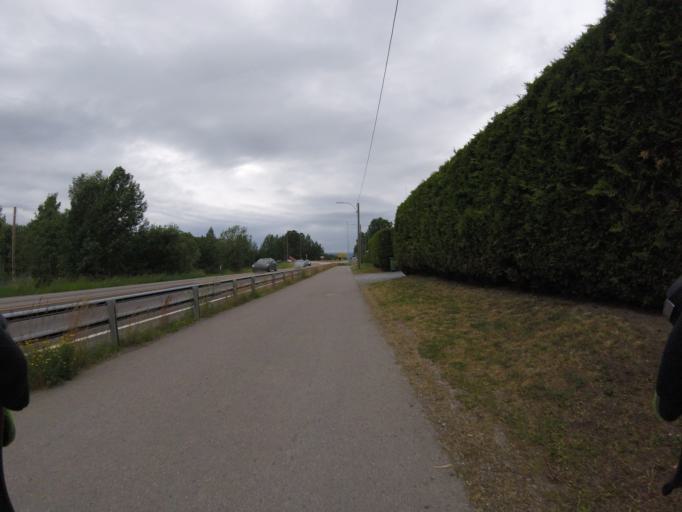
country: NO
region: Akershus
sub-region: Skedsmo
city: Lillestrom
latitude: 59.9756
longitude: 11.0273
